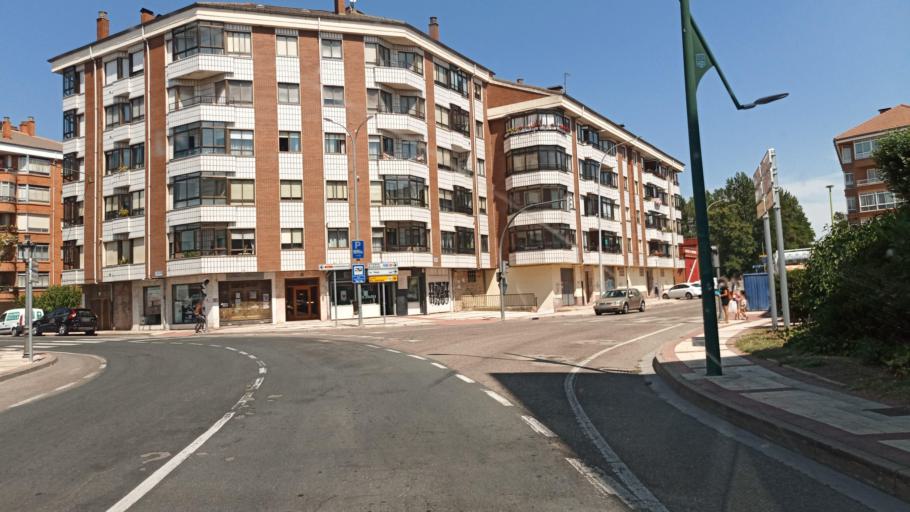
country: ES
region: Castille and Leon
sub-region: Provincia de Burgos
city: Briviesca
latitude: 42.5507
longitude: -3.3207
